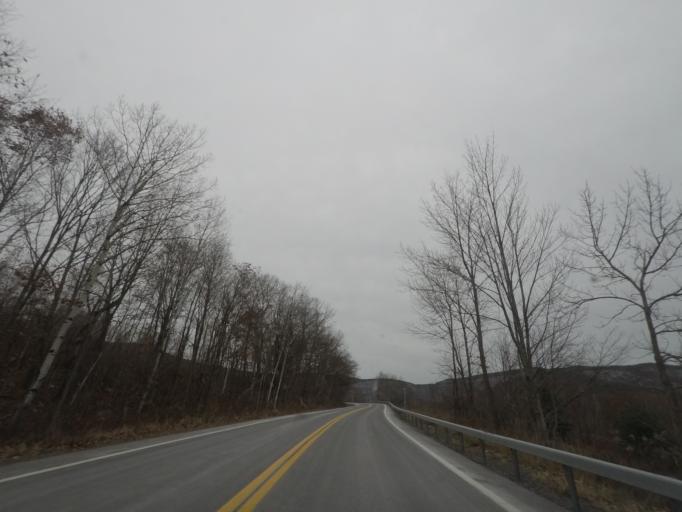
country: US
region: Massachusetts
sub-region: Berkshire County
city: Williamstown
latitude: 42.7415
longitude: -73.3016
